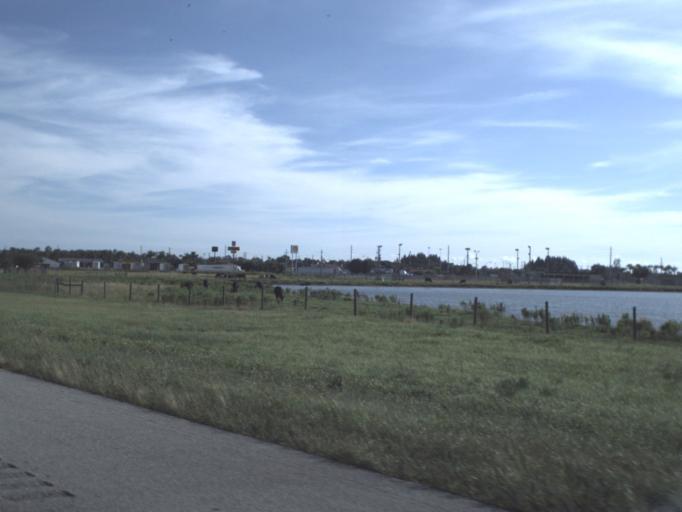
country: US
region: Florida
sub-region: Charlotte County
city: Charlotte Park
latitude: 26.9007
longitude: -82.0074
